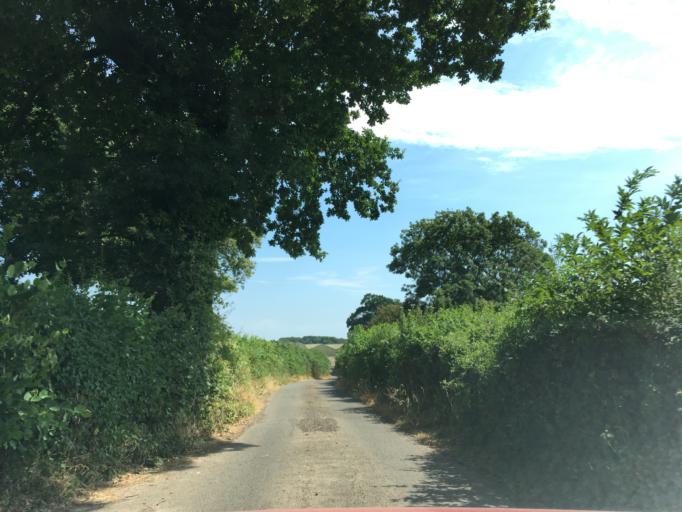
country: GB
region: Wales
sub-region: Monmouthshire
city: Magor
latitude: 51.5959
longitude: -2.8401
